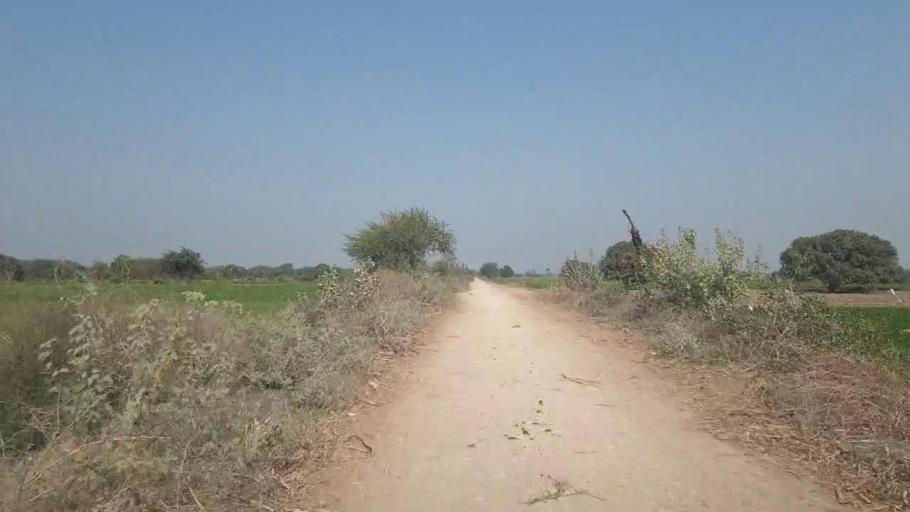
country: PK
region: Sindh
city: Tando Allahyar
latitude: 25.4411
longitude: 68.8499
